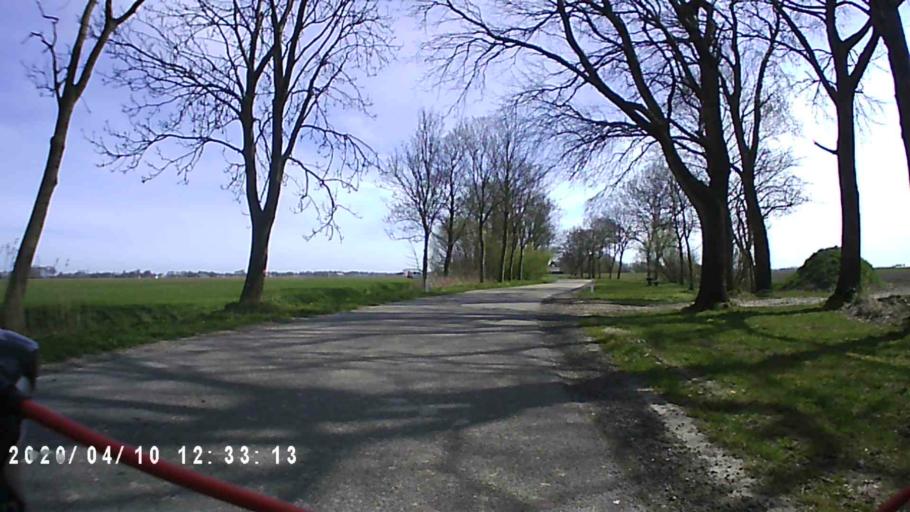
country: NL
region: Groningen
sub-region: Gemeente De Marne
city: Ulrum
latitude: 53.3954
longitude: 6.4144
